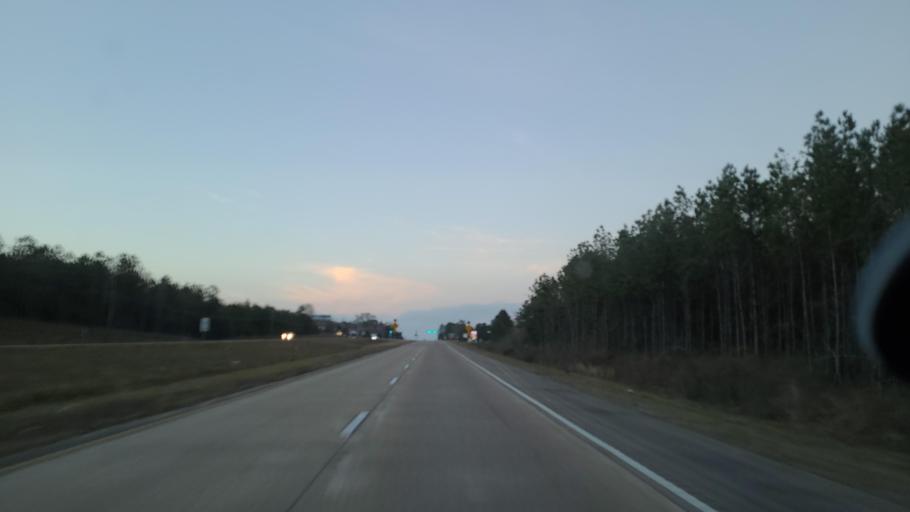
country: US
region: Mississippi
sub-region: Forrest County
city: Hattiesburg
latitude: 31.1828
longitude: -89.2496
